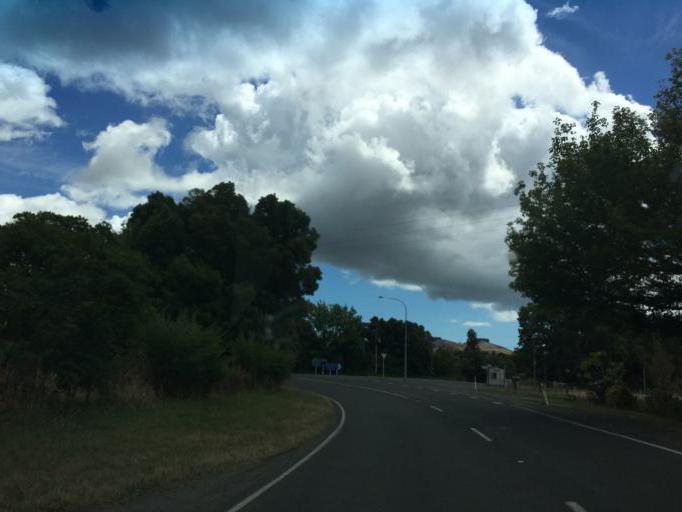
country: NZ
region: Hawke's Bay
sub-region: Hastings District
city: Hastings
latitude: -39.7183
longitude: 176.9293
